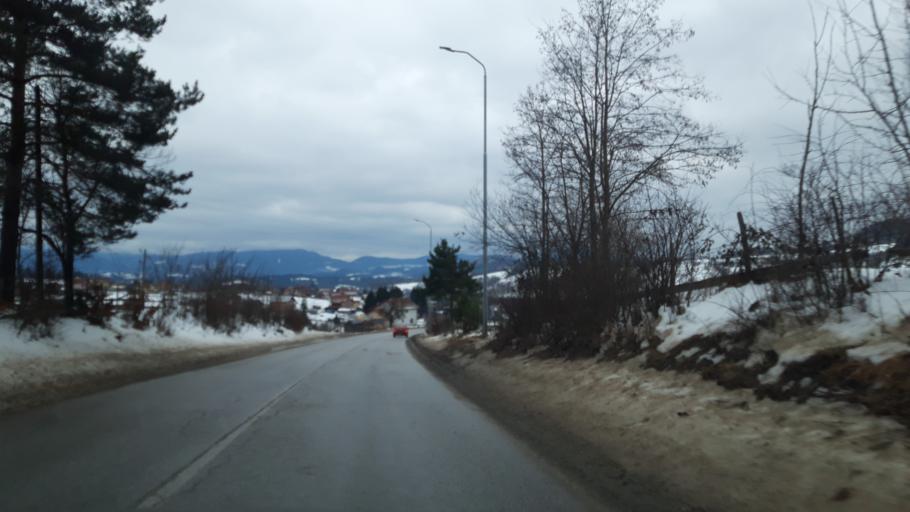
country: BA
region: Republika Srpska
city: Pale
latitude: 43.8890
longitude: 18.6166
